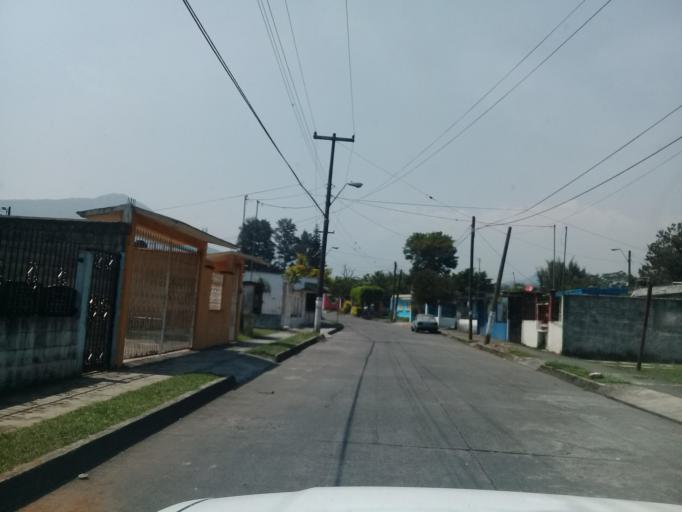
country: MX
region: Veracruz
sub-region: Ixtaczoquitlan
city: Buenavista
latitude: 18.8764
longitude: -97.0504
